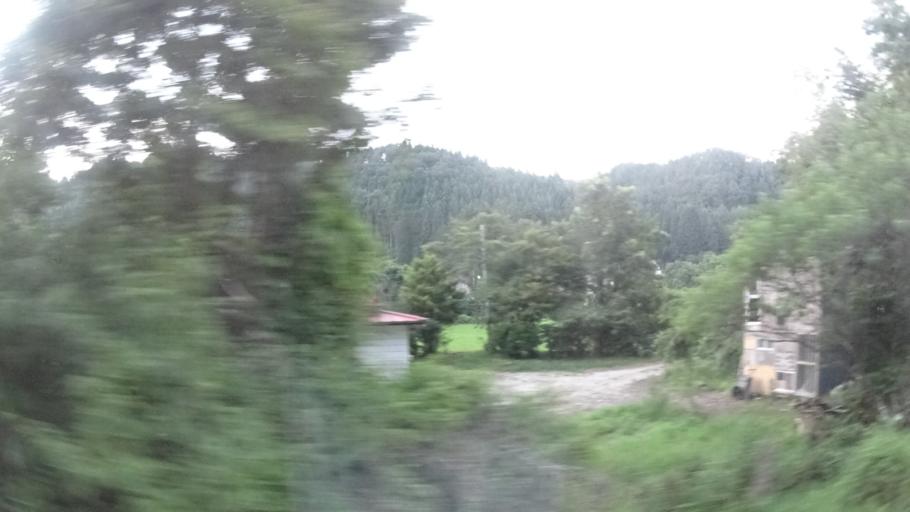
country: JP
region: Fukushima
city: Iwaki
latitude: 37.2066
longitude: 140.7478
